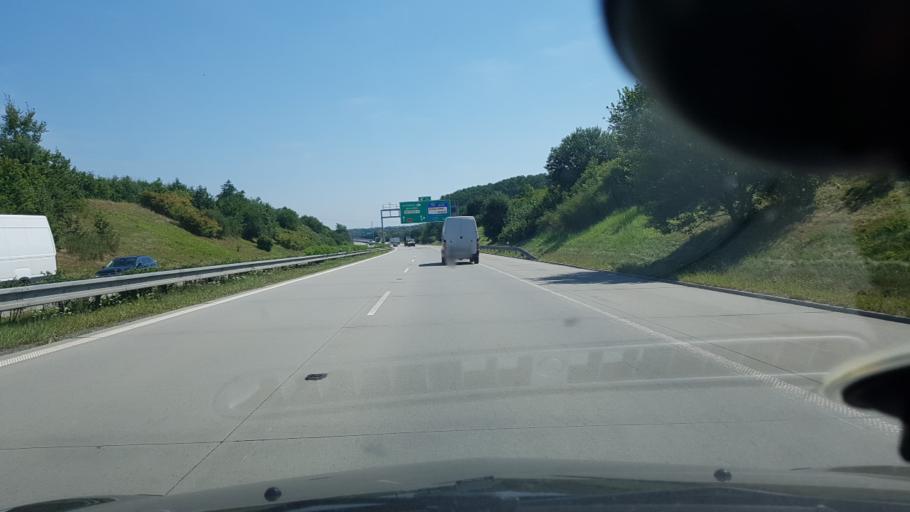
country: CZ
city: Klimkovice
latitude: 49.8013
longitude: 18.1859
